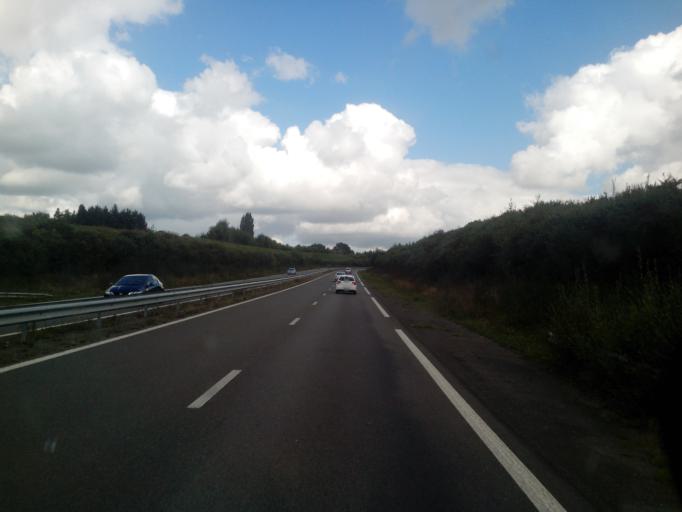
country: FR
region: Brittany
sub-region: Departement d'Ille-et-Vilaine
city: Chevaigne
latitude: 48.2049
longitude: -1.6220
